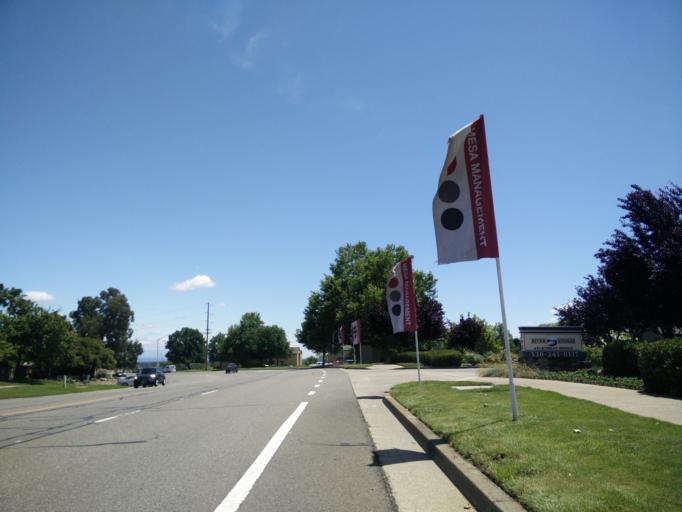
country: US
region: California
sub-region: Shasta County
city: Redding
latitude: 40.5987
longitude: -122.3710
